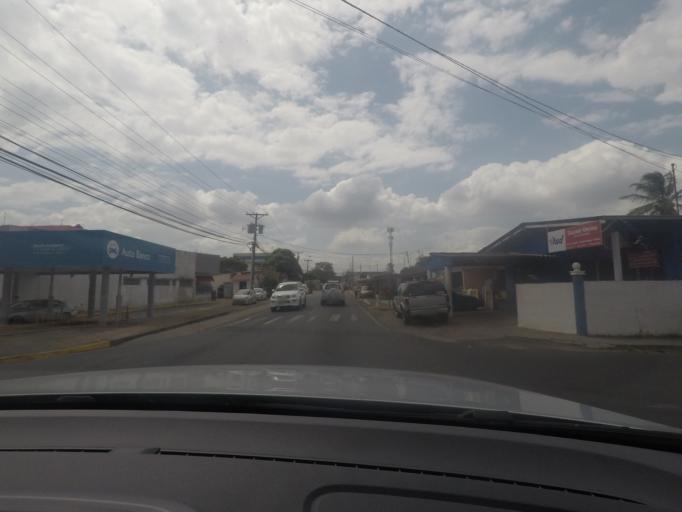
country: PA
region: Panama
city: La Chorrera
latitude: 8.8768
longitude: -79.7879
